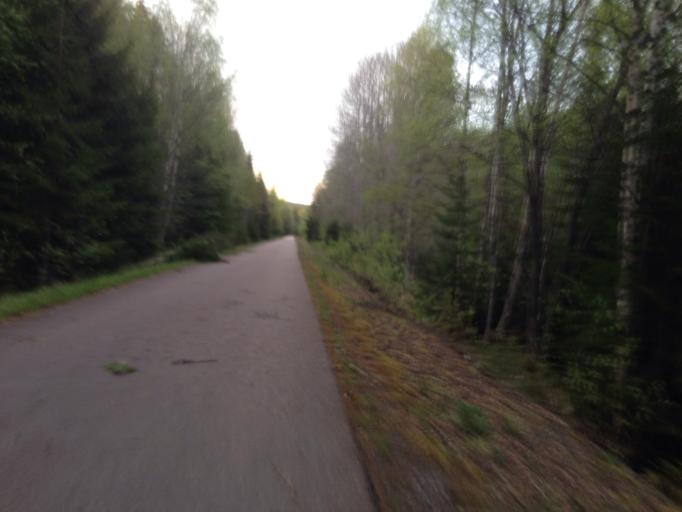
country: SE
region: Dalarna
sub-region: Ludvika Kommun
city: Grangesberg
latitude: 60.1277
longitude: 15.0702
